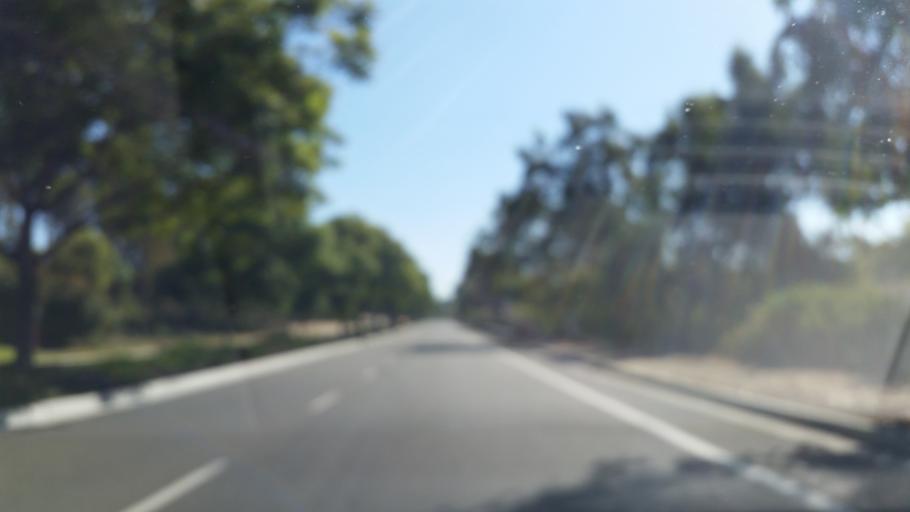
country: US
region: California
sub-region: Orange County
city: Irvine
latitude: 33.6572
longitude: -117.8261
